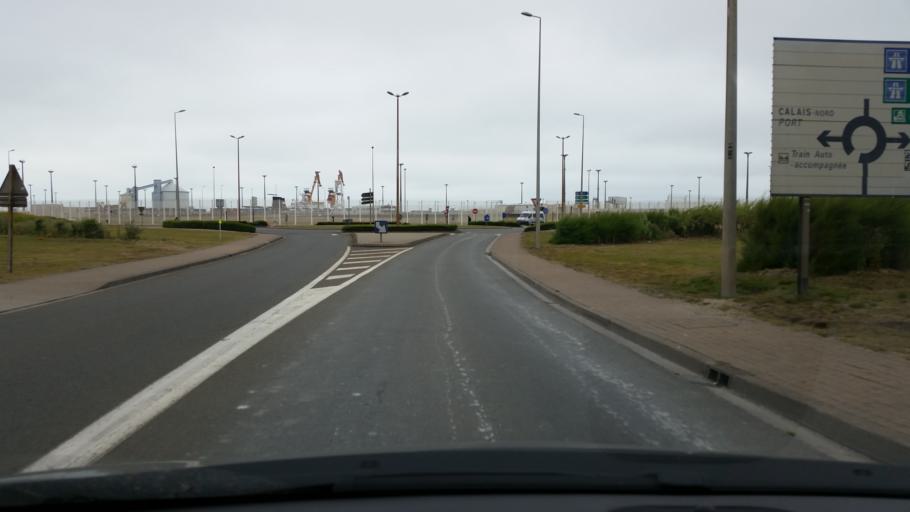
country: FR
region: Nord-Pas-de-Calais
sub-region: Departement du Pas-de-Calais
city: Calais
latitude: 50.9662
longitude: 1.8738
